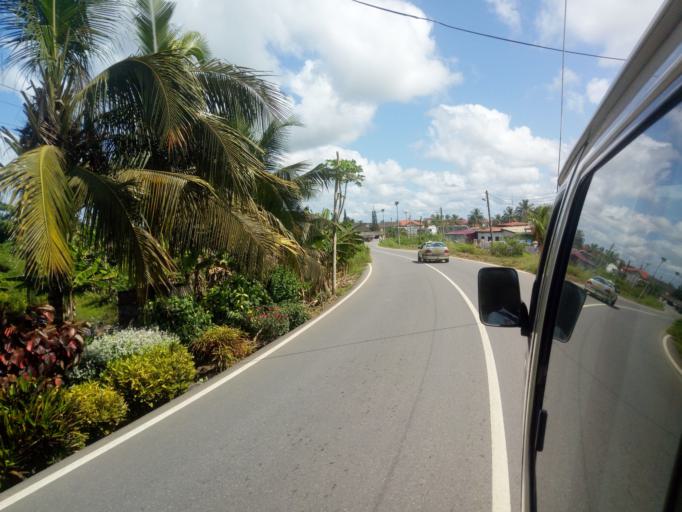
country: GH
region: Central
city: Elmina
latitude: 5.0952
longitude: -1.3353
